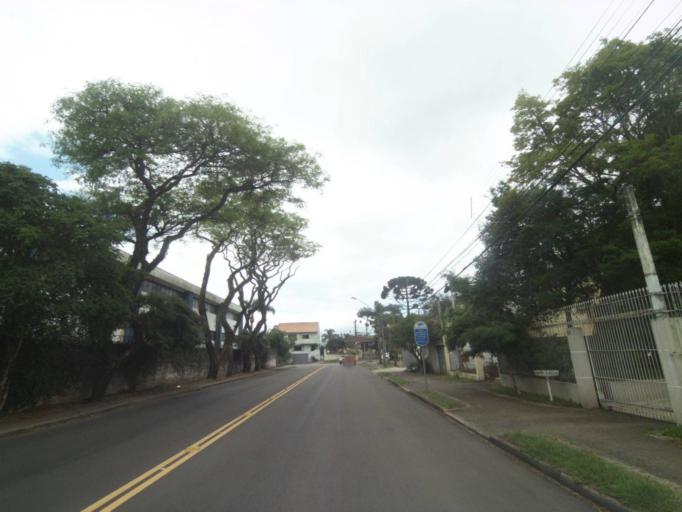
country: BR
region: Parana
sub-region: Pinhais
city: Pinhais
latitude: -25.4086
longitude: -49.2214
